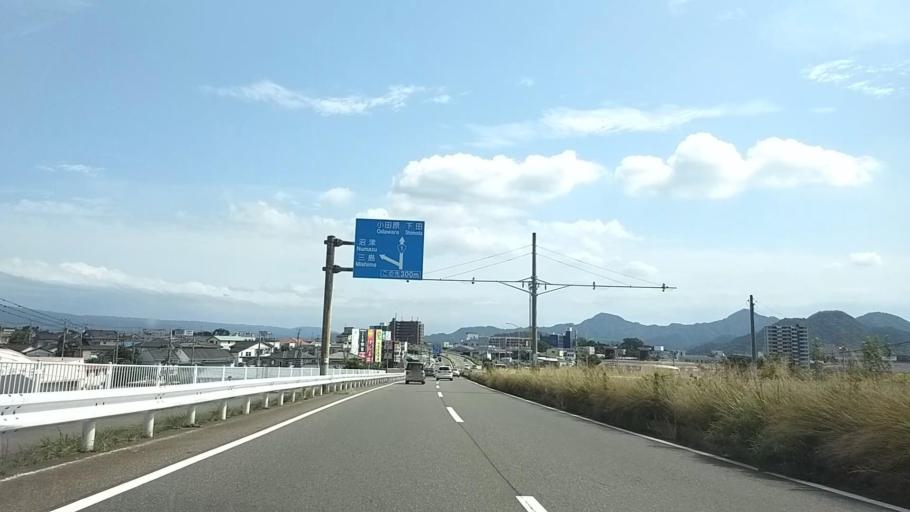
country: JP
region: Shizuoka
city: Mishima
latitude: 35.1149
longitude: 138.8906
